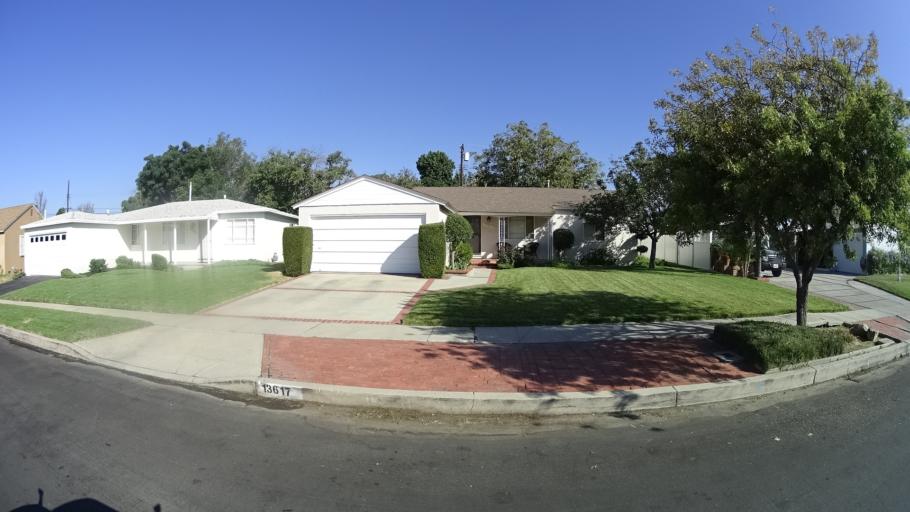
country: US
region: California
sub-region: Los Angeles County
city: Van Nuys
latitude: 34.2261
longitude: -118.4291
